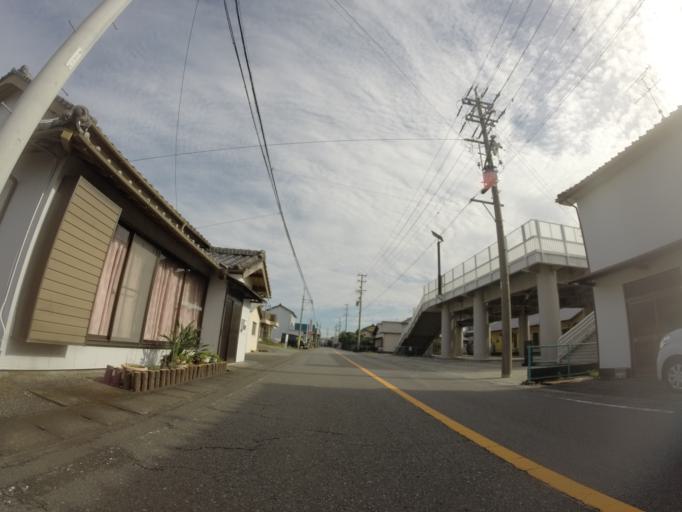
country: JP
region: Shizuoka
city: Sagara
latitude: 34.7541
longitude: 138.2482
